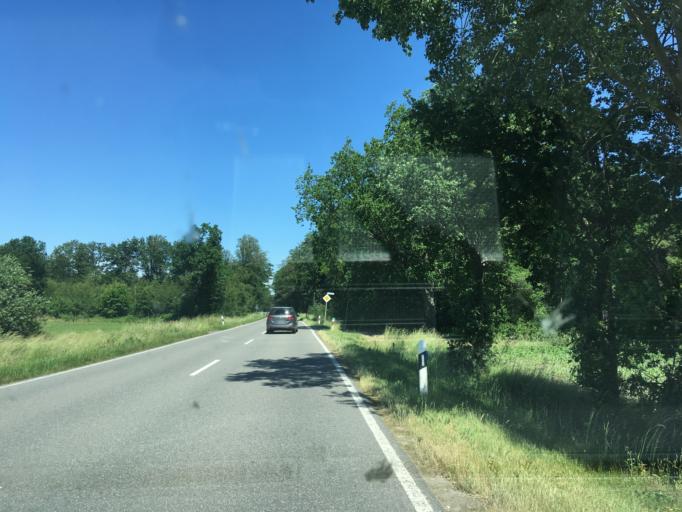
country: DE
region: North Rhine-Westphalia
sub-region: Regierungsbezirk Munster
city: Borken
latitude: 51.8105
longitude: 6.8156
